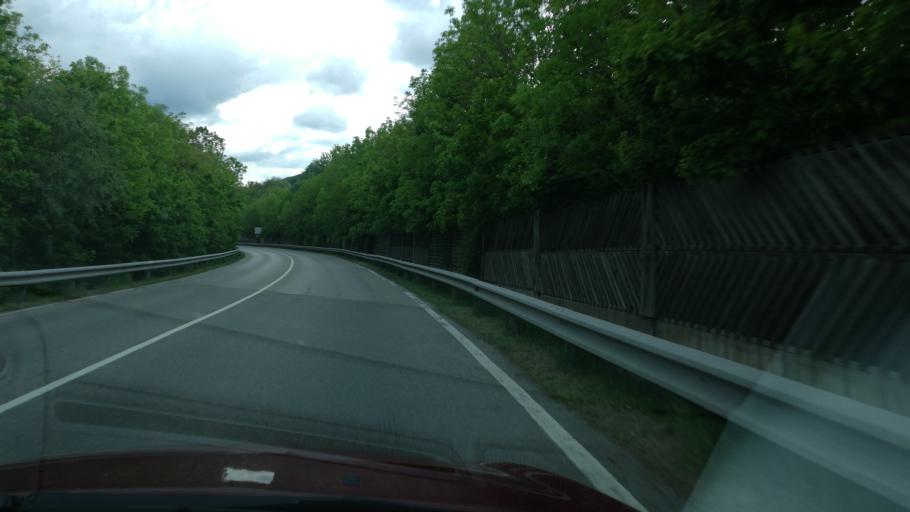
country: AT
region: Lower Austria
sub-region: Politischer Bezirk Baden
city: Baden
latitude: 48.0074
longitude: 16.2118
